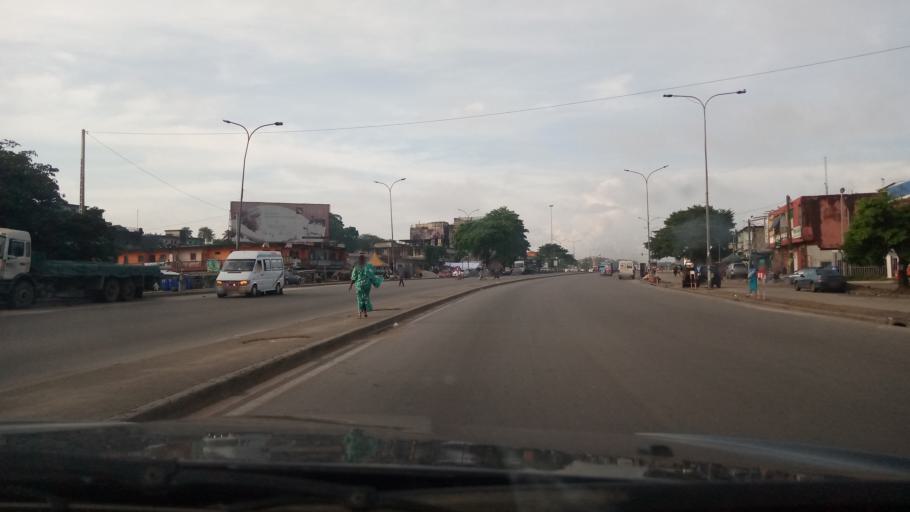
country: CI
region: Lagunes
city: Abobo
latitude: 5.4153
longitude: -4.0163
